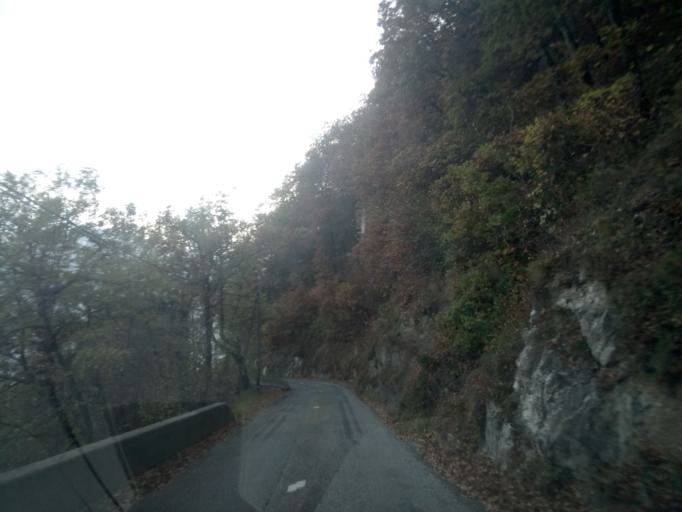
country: FR
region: Rhone-Alpes
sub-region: Departement de la Savoie
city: La Chambre
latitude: 45.3768
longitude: 6.3080
